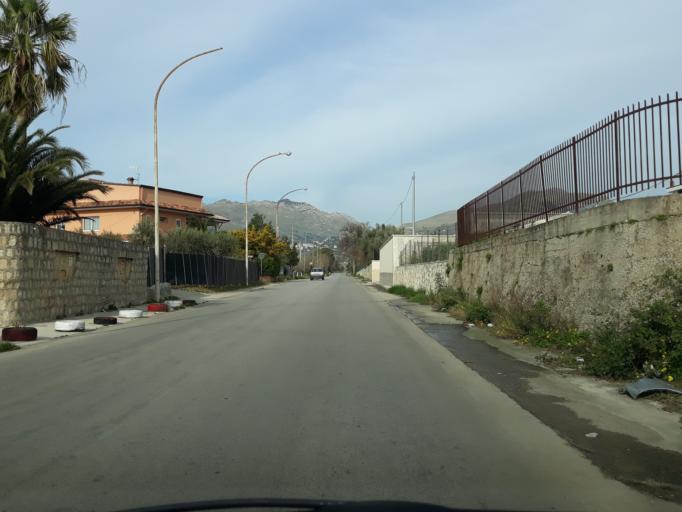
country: IT
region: Sicily
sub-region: Palermo
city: Borgetto
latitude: 38.0635
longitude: 13.1439
